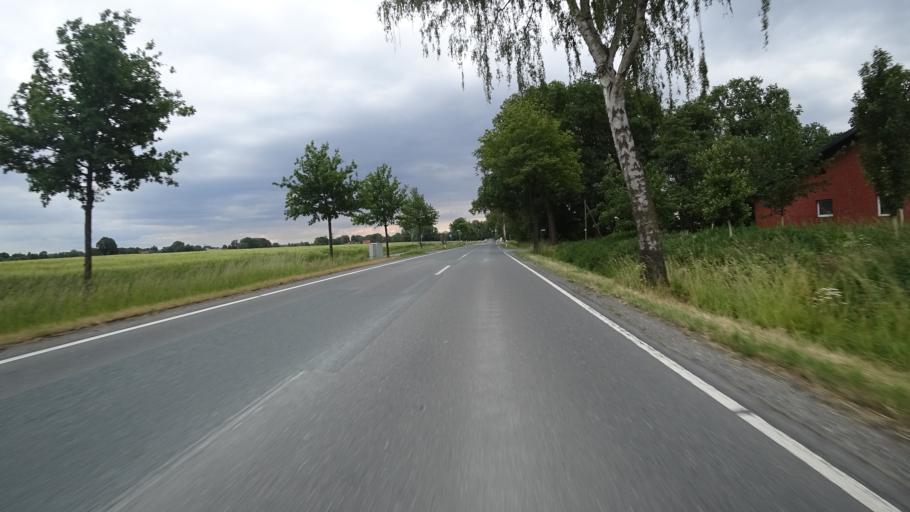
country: DE
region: North Rhine-Westphalia
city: Rietberg
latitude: 51.8351
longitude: 8.4142
